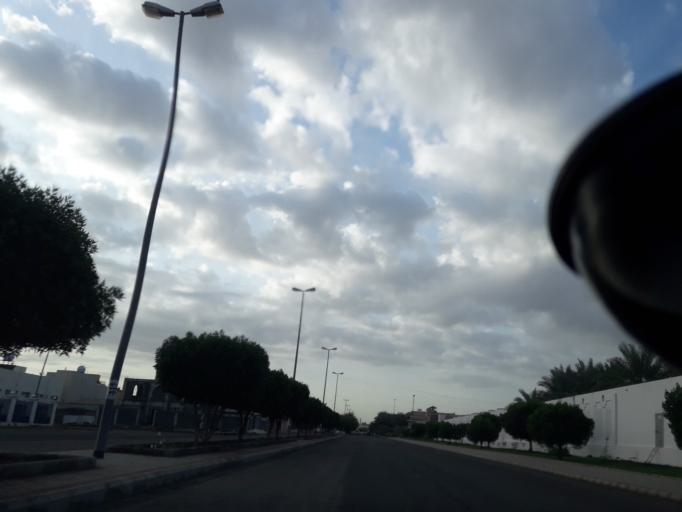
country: SA
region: Al Madinah al Munawwarah
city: Medina
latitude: 24.4257
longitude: 39.6269
